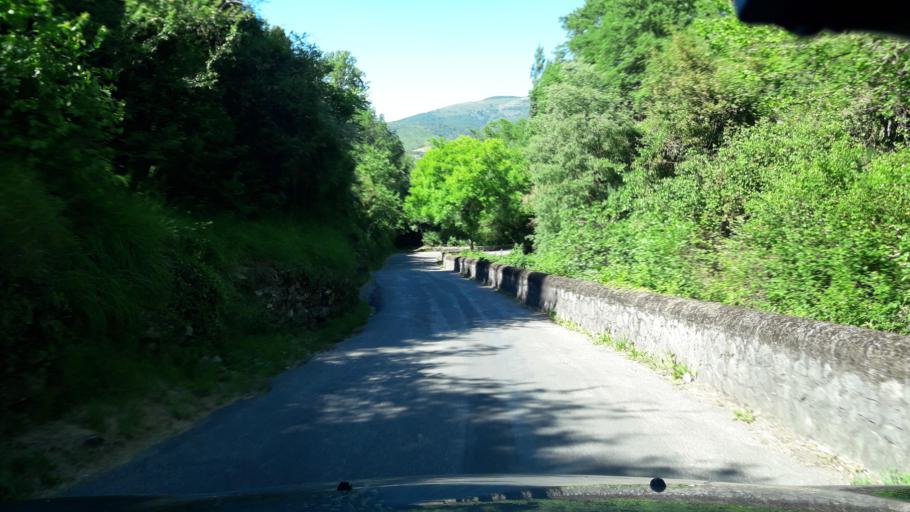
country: FR
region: Rhone-Alpes
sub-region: Departement de l'Ardeche
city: Coux
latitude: 44.7304
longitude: 4.6179
